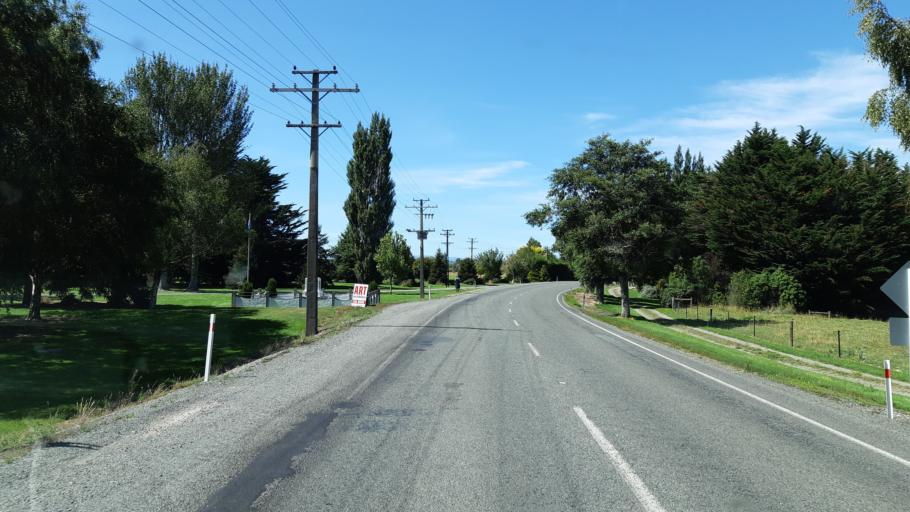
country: NZ
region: Southland
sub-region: Gore District
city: Gore
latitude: -45.9926
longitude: 168.8097
